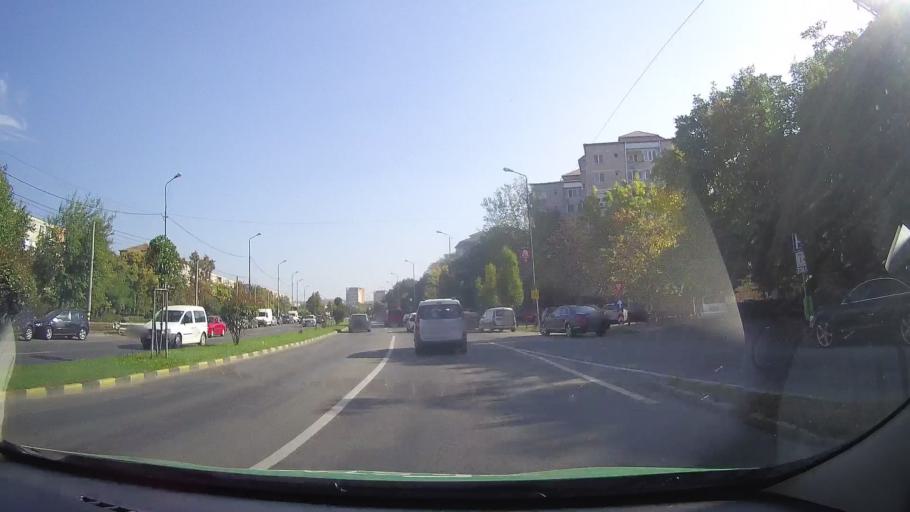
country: RO
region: Bihor
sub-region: Comuna Biharea
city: Oradea
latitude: 47.0737
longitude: 21.9092
